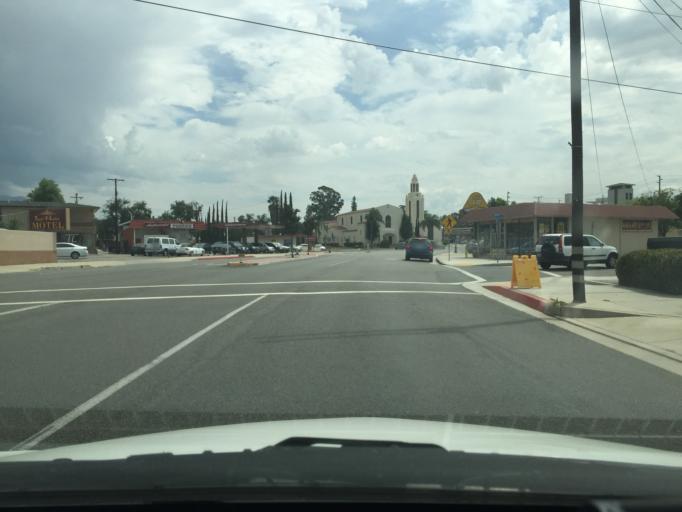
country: US
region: California
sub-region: San Bernardino County
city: Redlands
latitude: 34.0570
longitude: -117.1775
